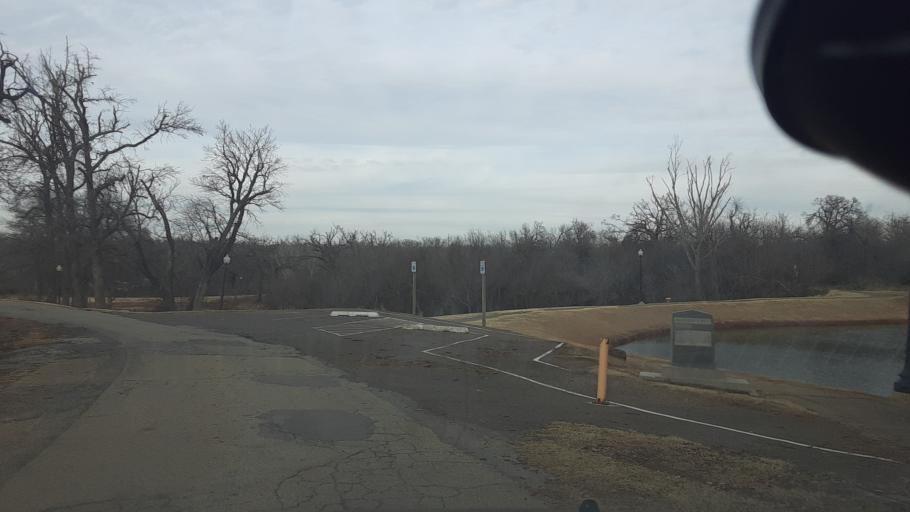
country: US
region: Oklahoma
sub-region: Logan County
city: Guthrie
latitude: 35.8829
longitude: -97.4112
